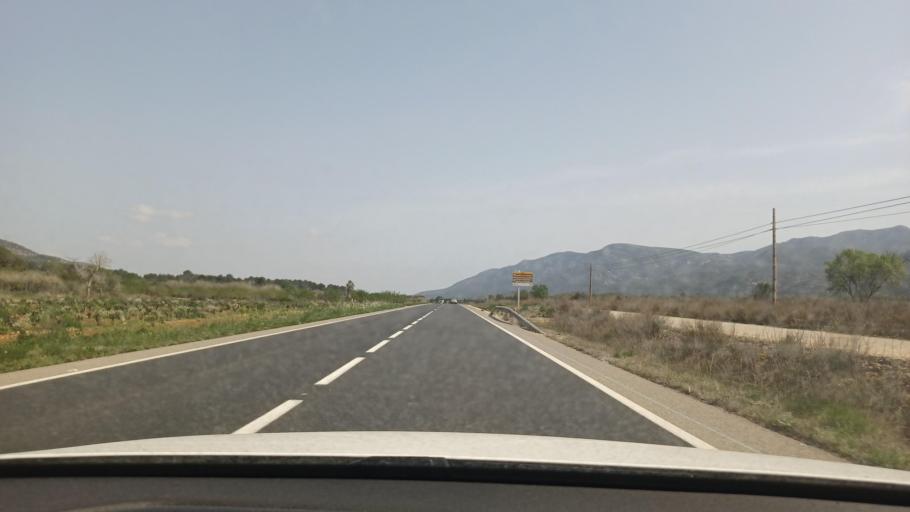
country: ES
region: Catalonia
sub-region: Provincia de Tarragona
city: Ulldecona
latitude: 40.6226
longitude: 0.4746
